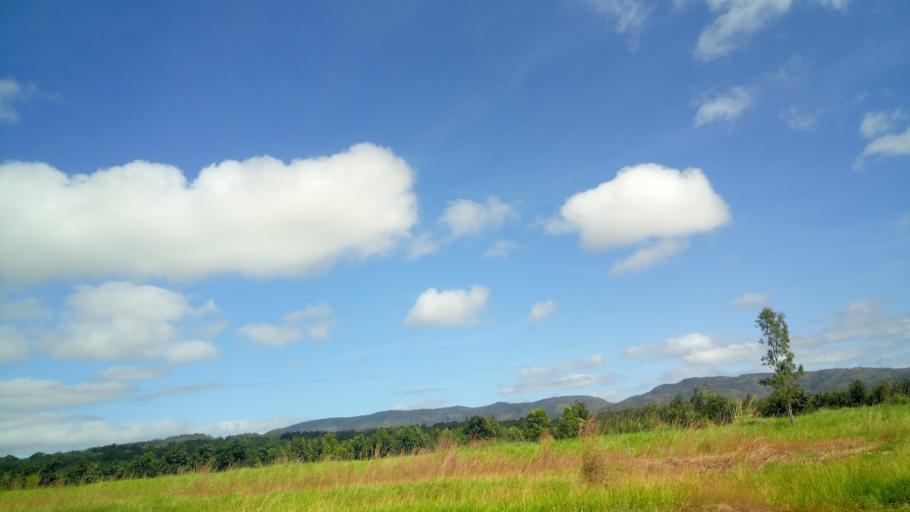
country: AU
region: Queensland
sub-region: Tablelands
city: Tolga
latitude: -17.1881
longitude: 145.4675
